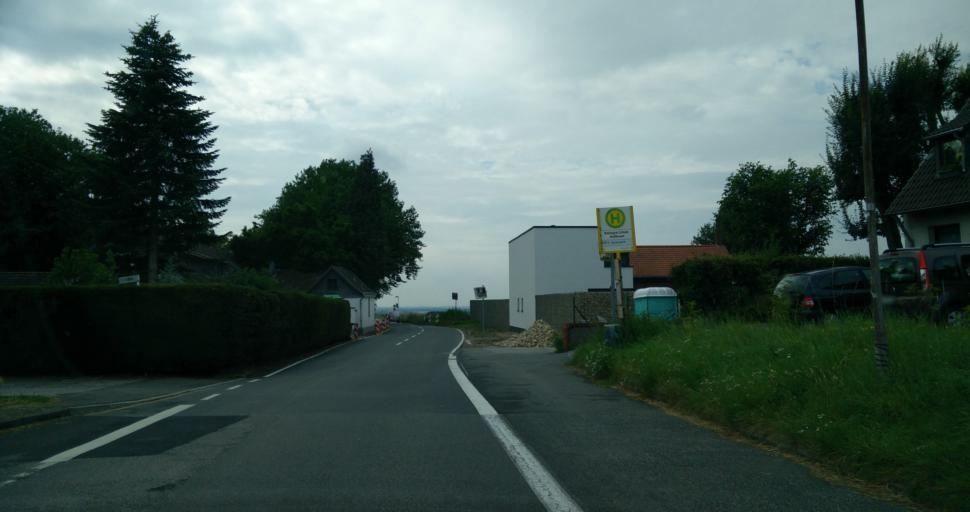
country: DE
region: North Rhine-Westphalia
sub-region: Regierungsbezirk Dusseldorf
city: Erkrath
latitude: 51.2753
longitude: 6.9047
